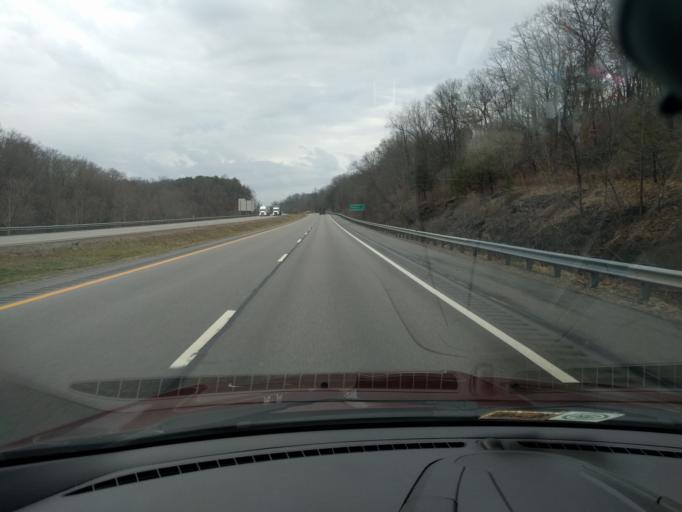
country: US
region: West Virginia
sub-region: Wood County
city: Boaz
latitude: 39.3212
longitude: -81.4706
